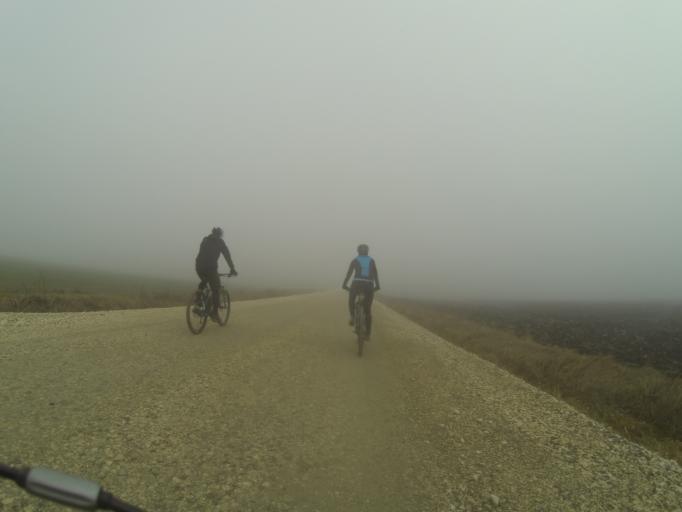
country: RO
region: Mehedinti
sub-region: Comuna Balacita
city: Gvardinita
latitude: 44.4333
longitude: 23.1336
